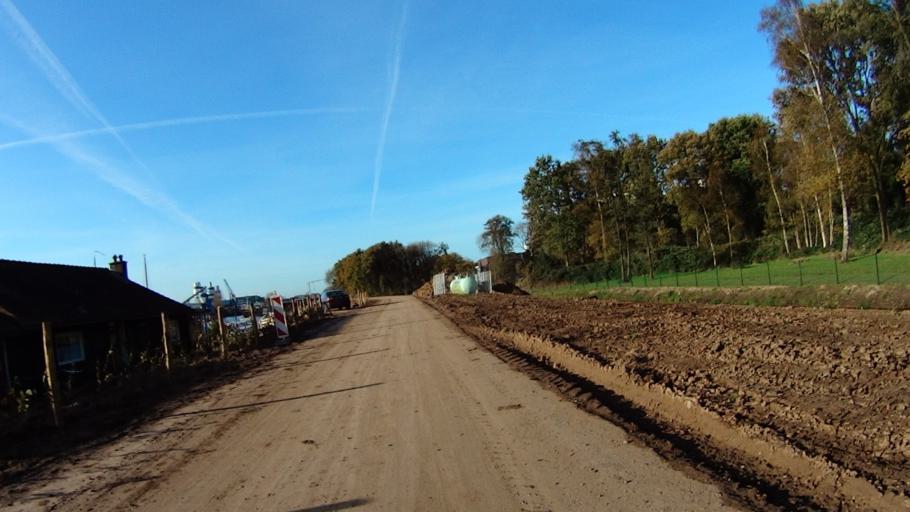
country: NL
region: Utrecht
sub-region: Gemeente Amersfoort
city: Hoogland
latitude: 52.1681
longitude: 5.3713
